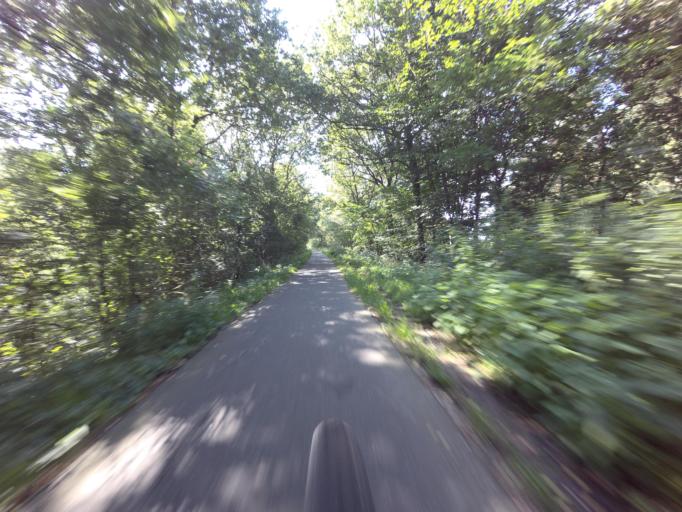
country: DK
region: Central Jutland
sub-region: Viborg Kommune
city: Viborg
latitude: 56.4129
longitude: 9.3641
